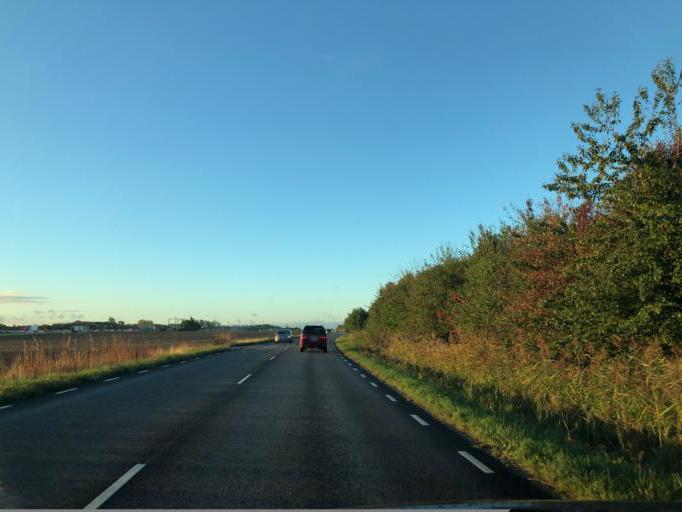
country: SE
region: Skane
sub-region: Lomma Kommun
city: Lomma
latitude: 55.6791
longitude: 13.0960
